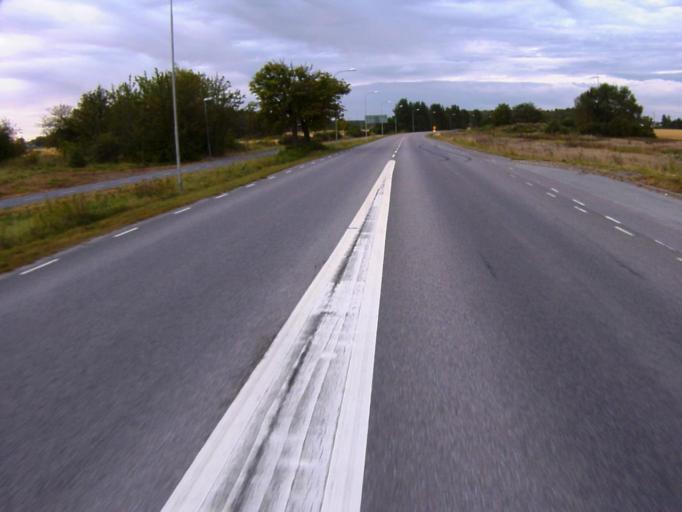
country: SE
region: Soedermanland
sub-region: Eskilstuna Kommun
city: Torshalla
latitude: 59.4068
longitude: 16.4799
